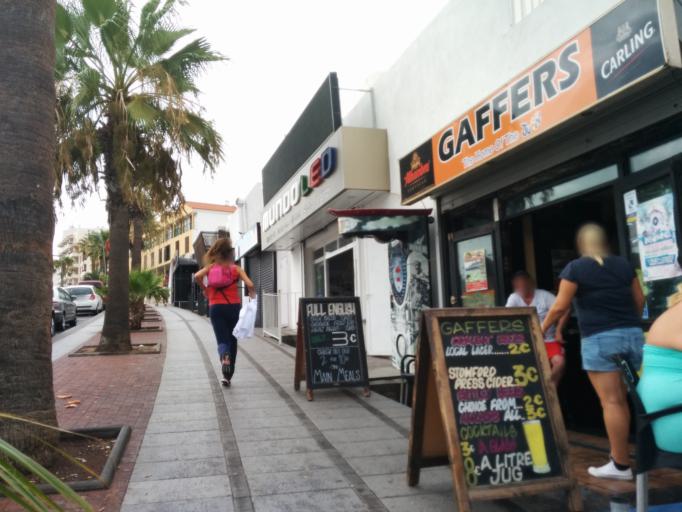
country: ES
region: Canary Islands
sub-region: Provincia de Santa Cruz de Tenerife
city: Playa de las Americas
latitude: 28.0657
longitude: -16.7279
